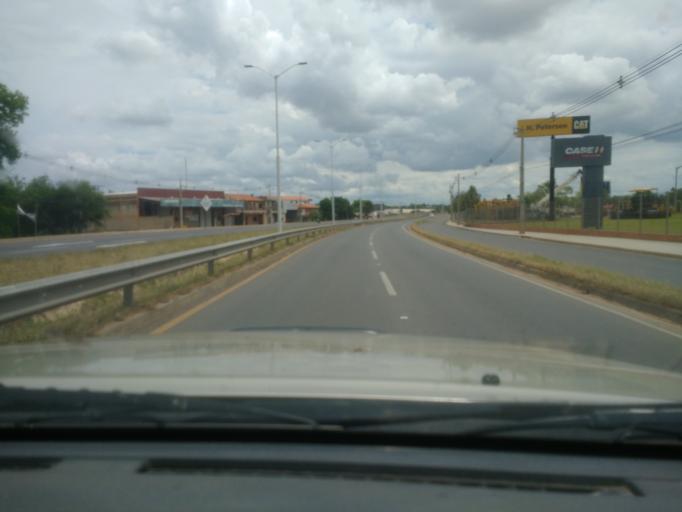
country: PY
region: Central
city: Limpio
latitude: -25.1881
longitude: -57.4971
